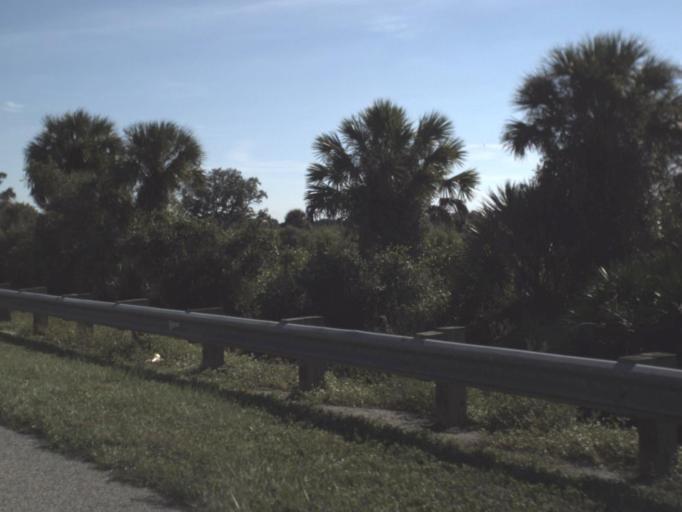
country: US
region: Florida
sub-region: Glades County
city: Moore Haven
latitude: 26.8758
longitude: -81.2238
